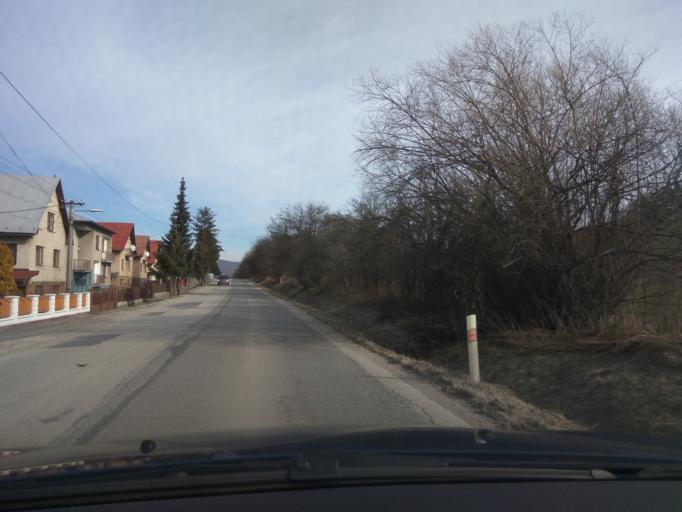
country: SK
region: Zilinsky
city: Rajec
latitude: 49.0871
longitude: 18.6255
